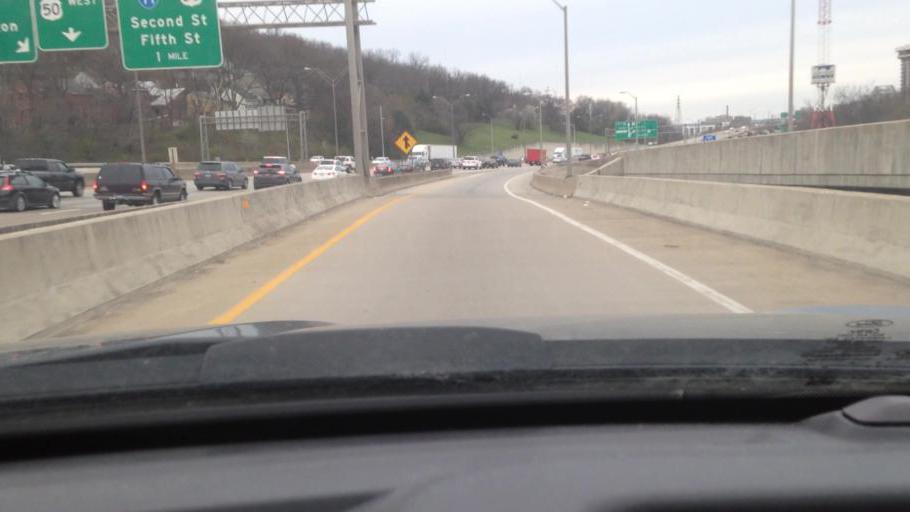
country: US
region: Kentucky
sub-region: Kenton County
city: Park Hills
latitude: 39.0789
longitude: -84.5218
